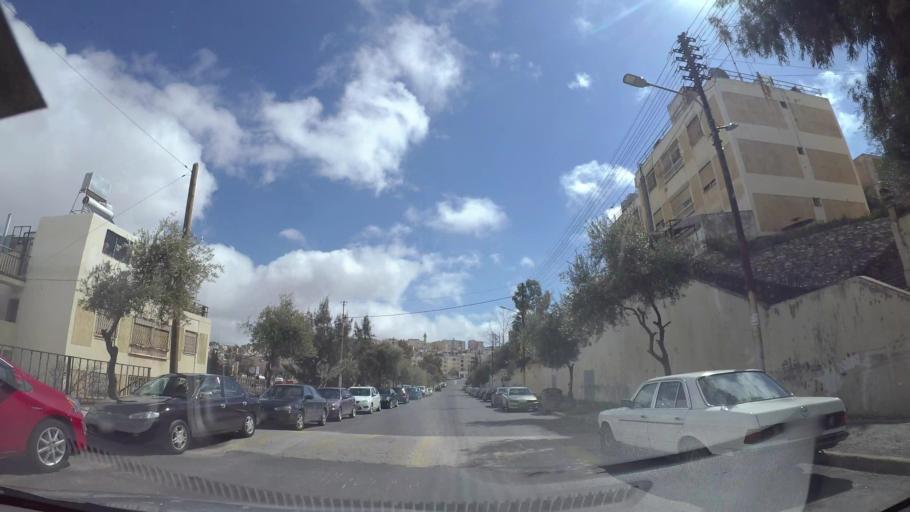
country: JO
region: Amman
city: Al Jubayhah
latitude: 32.0583
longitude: 35.8819
